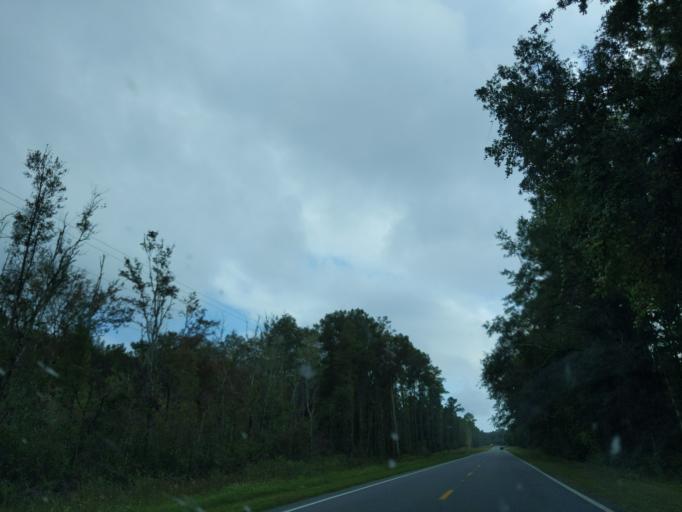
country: US
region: Florida
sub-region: Wakulla County
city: Crawfordville
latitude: 30.1280
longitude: -84.3148
